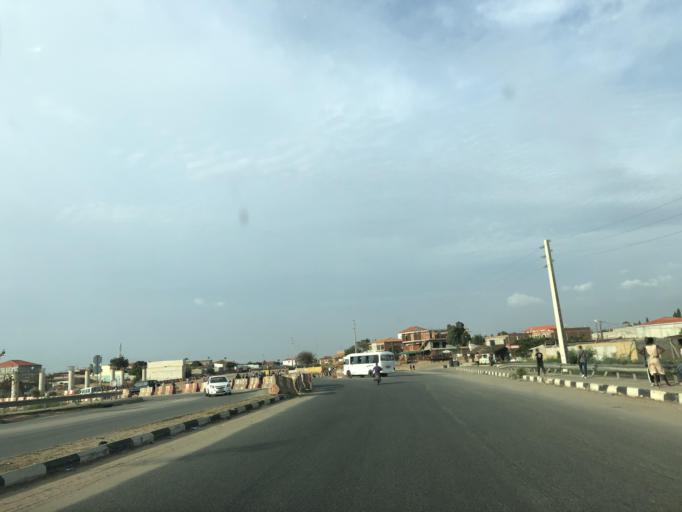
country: AO
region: Luanda
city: Luanda
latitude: -8.9299
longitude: 13.3028
